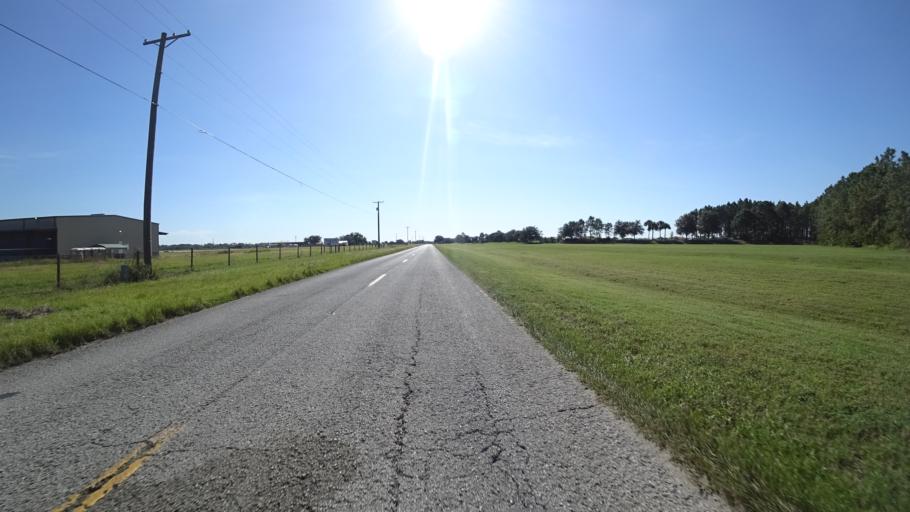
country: US
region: Florida
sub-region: Hillsborough County
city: Sun City Center
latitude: 27.6630
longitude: -82.3314
